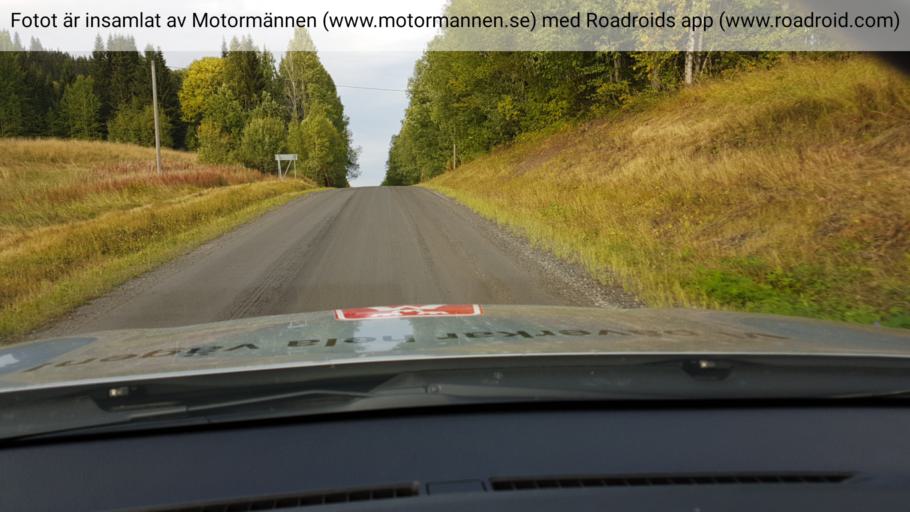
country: SE
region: Jaemtland
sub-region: Stroemsunds Kommun
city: Stroemsund
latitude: 64.0887
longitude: 15.8248
